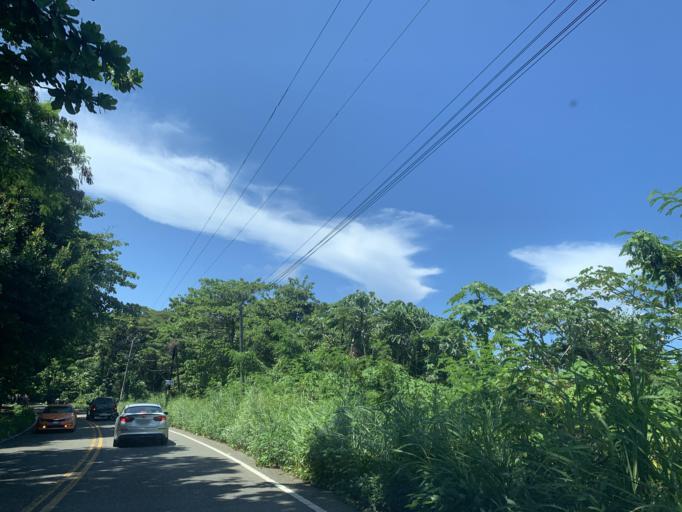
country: DO
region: Maria Trinidad Sanchez
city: Cabrera
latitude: 19.6546
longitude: -69.9342
